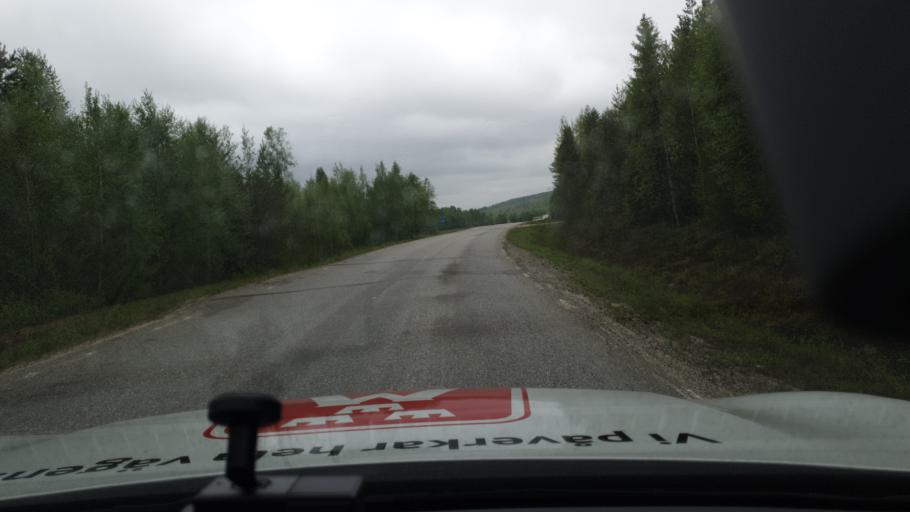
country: SE
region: Vaesterbotten
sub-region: Vannas Kommun
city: Vannasby
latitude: 64.0395
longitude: 19.9311
